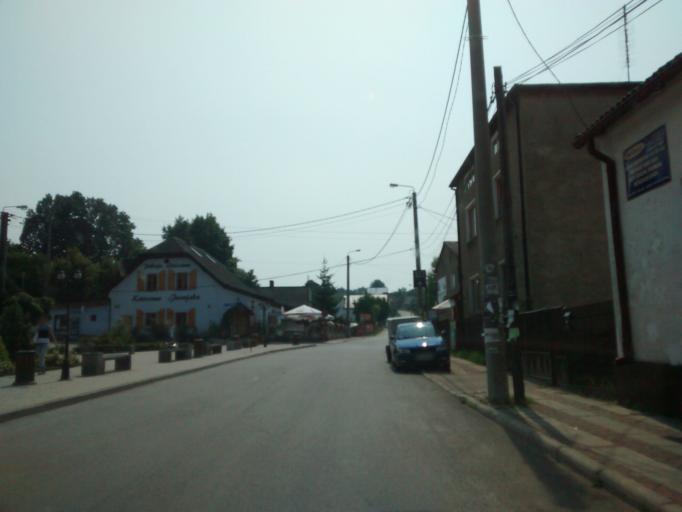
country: PL
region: Silesian Voivodeship
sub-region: Powiat zawiercianski
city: Ogrodzieniec
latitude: 50.4543
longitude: 19.5478
